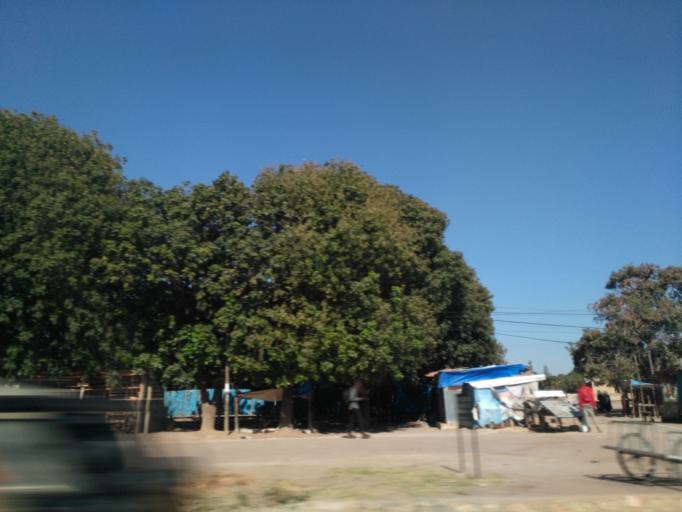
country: TZ
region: Dodoma
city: Dodoma
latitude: -6.1388
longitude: 35.7467
